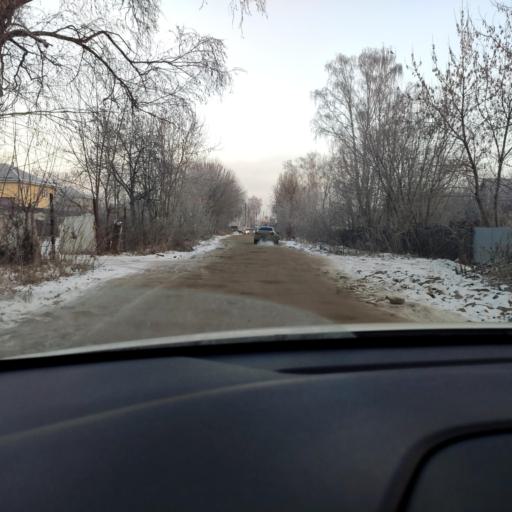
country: RU
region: Tatarstan
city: Staroye Arakchino
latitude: 55.8647
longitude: 49.0468
